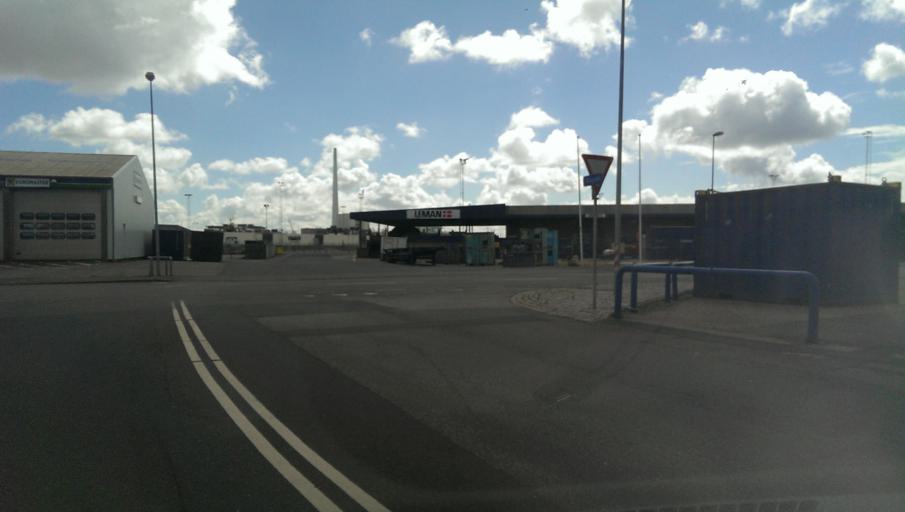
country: DK
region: South Denmark
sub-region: Esbjerg Kommune
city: Esbjerg
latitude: 55.4661
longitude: 8.4382
